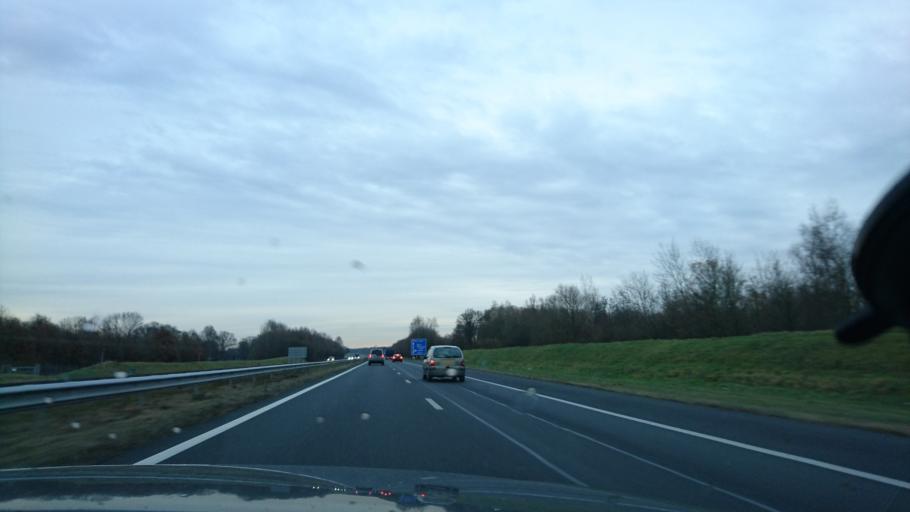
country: NL
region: Overijssel
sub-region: Gemeente Oldenzaal
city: Oldenzaal
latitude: 52.2910
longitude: 6.9117
